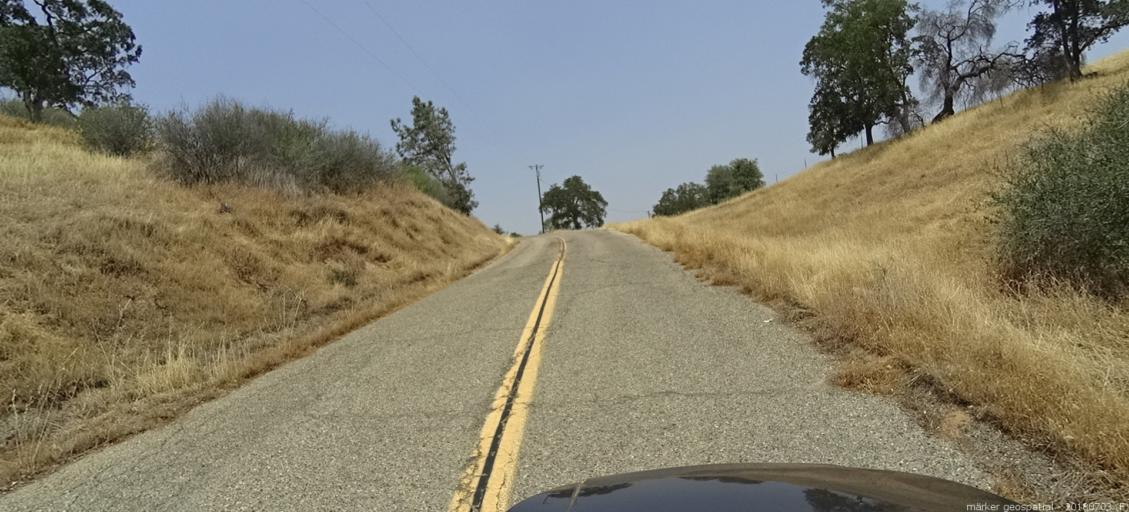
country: US
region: California
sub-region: Madera County
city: Yosemite Lakes
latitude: 37.0576
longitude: -119.6614
